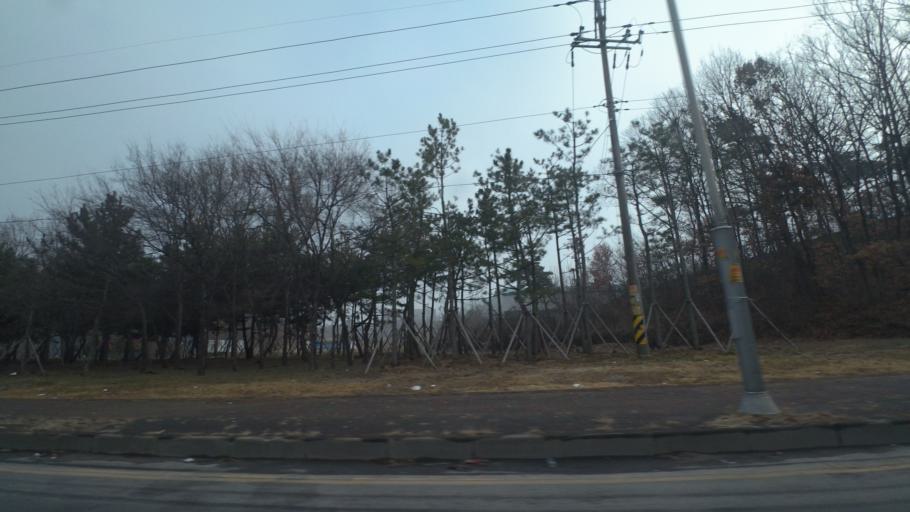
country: KR
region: Gyeonggi-do
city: Hwaseong-si
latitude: 36.9904
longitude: 126.8520
